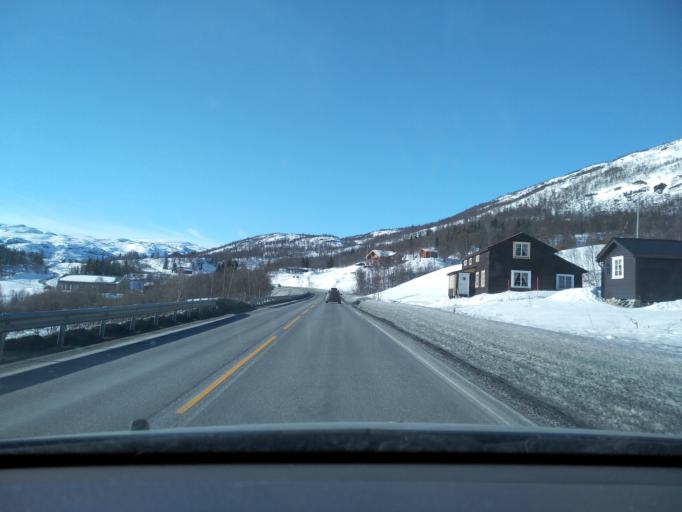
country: NO
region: Aust-Agder
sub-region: Bykle
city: Hovden
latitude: 59.7703
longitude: 7.3730
